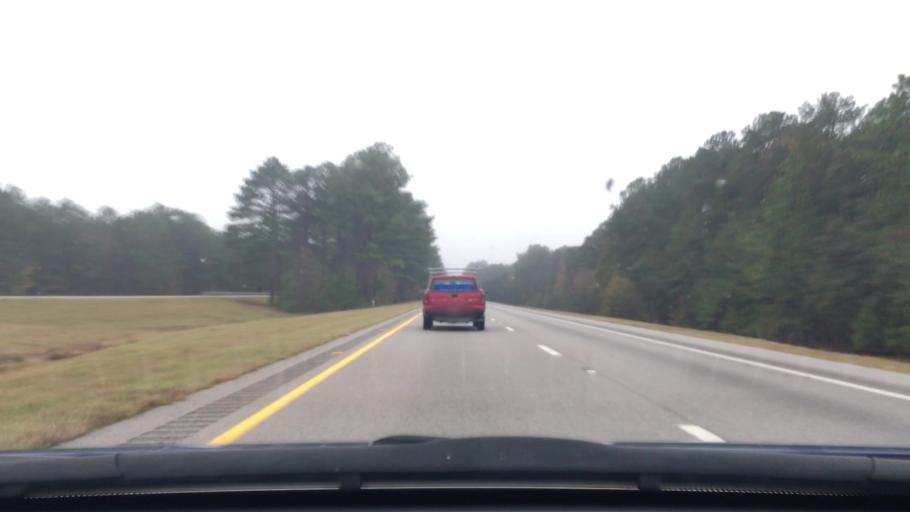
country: US
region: South Carolina
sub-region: Kershaw County
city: Camden
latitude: 34.2092
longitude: -80.4683
